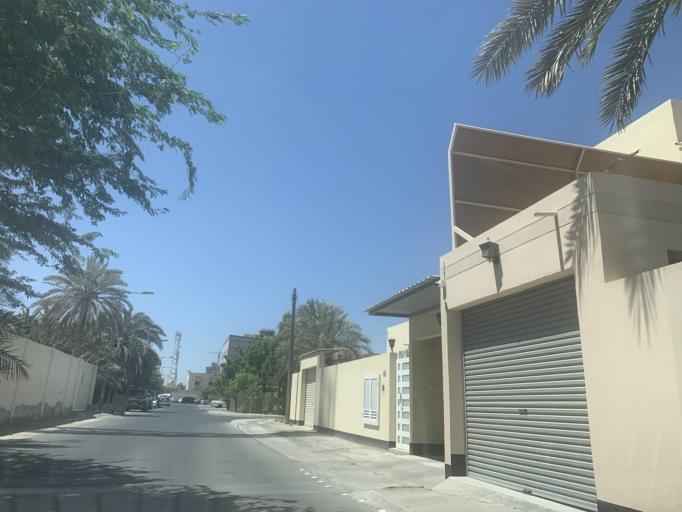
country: BH
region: Manama
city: Jidd Hafs
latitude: 26.2154
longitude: 50.4516
